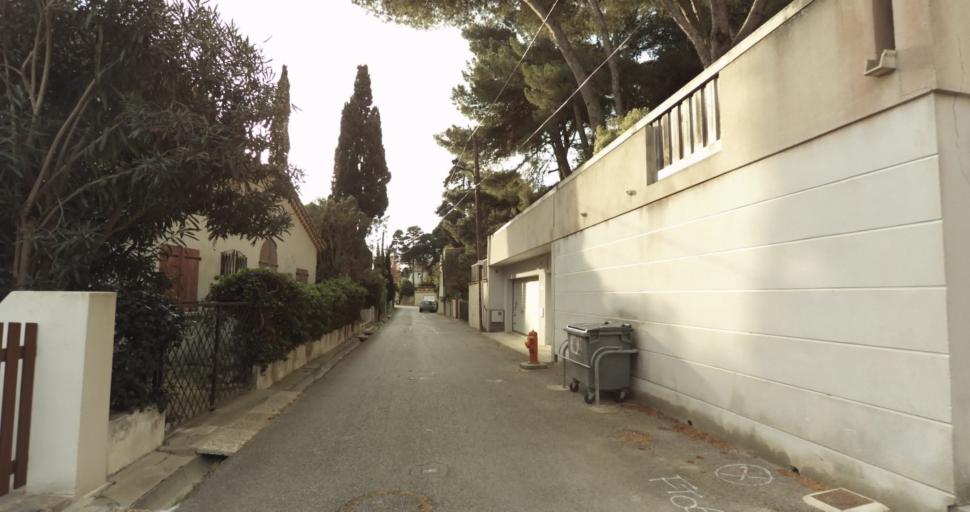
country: FR
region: Languedoc-Roussillon
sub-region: Departement de l'Aude
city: Leucate
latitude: 42.9318
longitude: 3.0348
